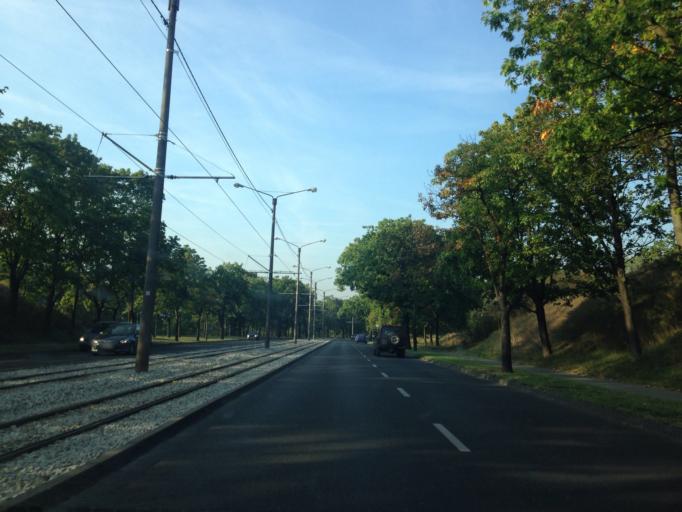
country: PL
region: Kujawsko-Pomorskie
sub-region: Torun
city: Torun
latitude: 53.0133
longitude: 18.6268
